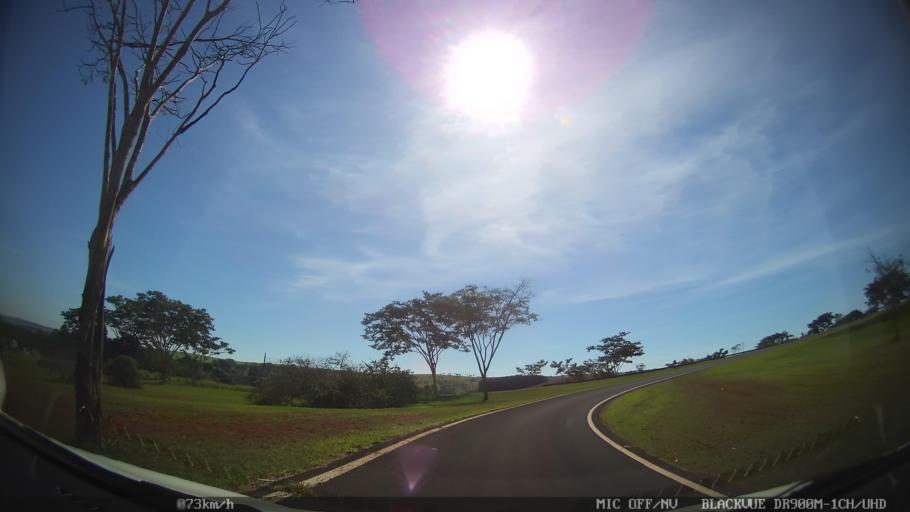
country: BR
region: Sao Paulo
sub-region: Santa Rita Do Passa Quatro
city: Santa Rita do Passa Quatro
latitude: -21.7552
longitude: -47.5645
